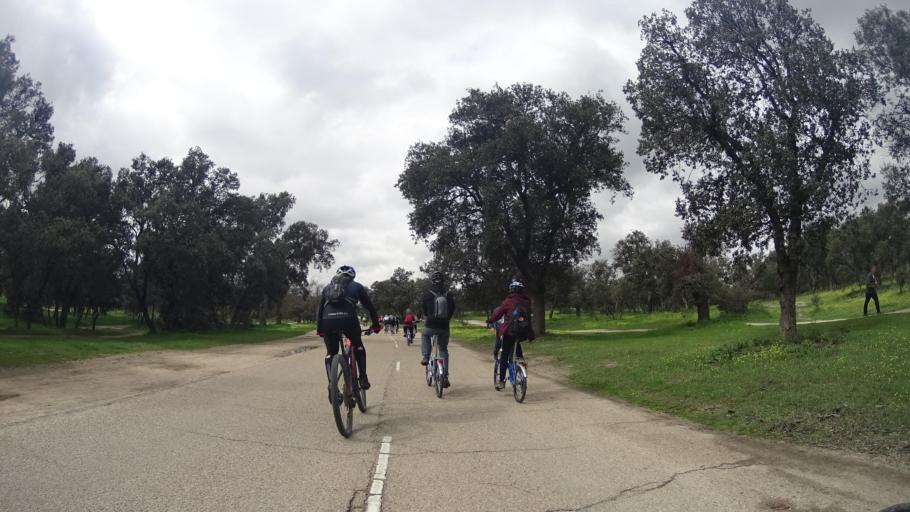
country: ES
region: Madrid
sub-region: Provincia de Madrid
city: Latina
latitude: 40.4148
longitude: -3.7547
